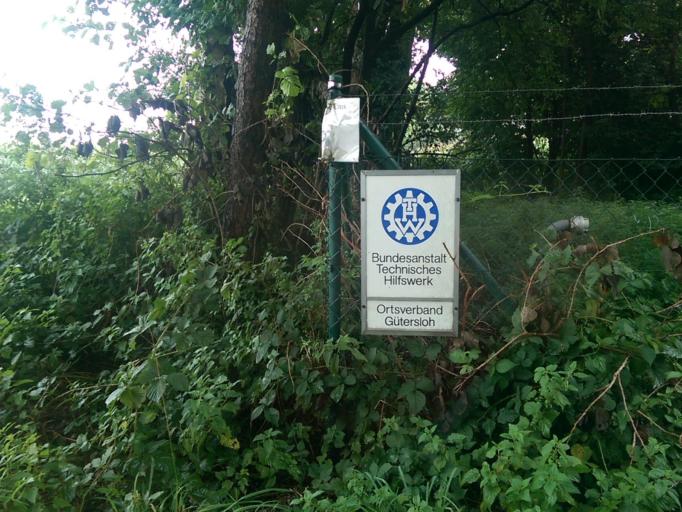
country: DE
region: North Rhine-Westphalia
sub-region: Regierungsbezirk Detmold
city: Guetersloh
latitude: 51.9337
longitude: 8.3151
